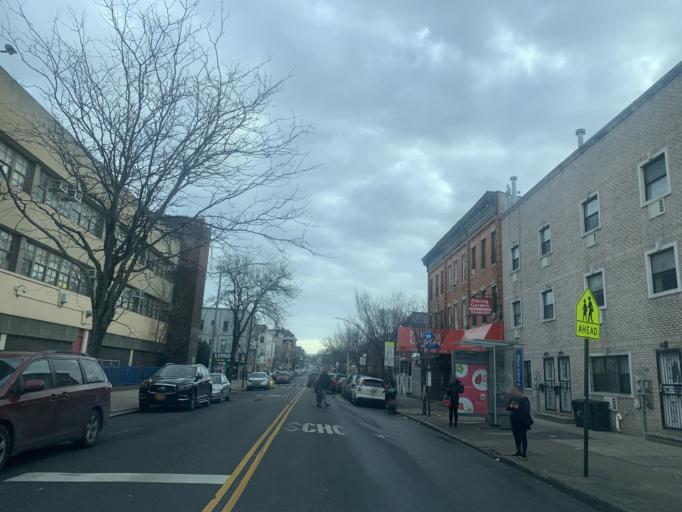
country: US
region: New York
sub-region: Kings County
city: East New York
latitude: 40.6953
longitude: -73.9163
